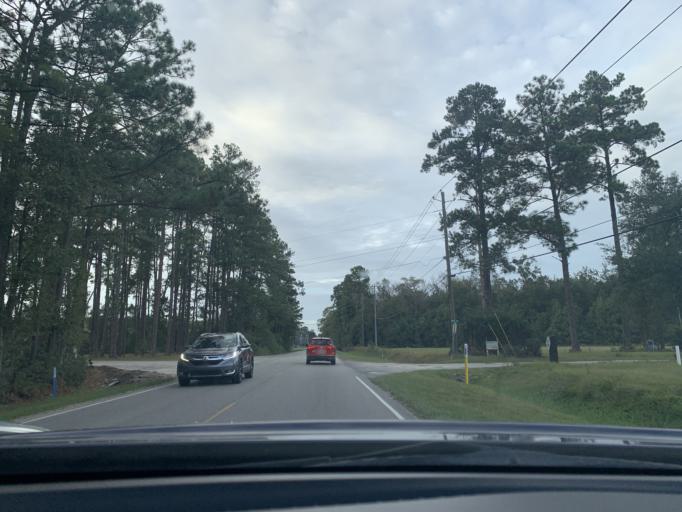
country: US
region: Georgia
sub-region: Chatham County
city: Pooler
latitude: 32.0516
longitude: -81.2660
